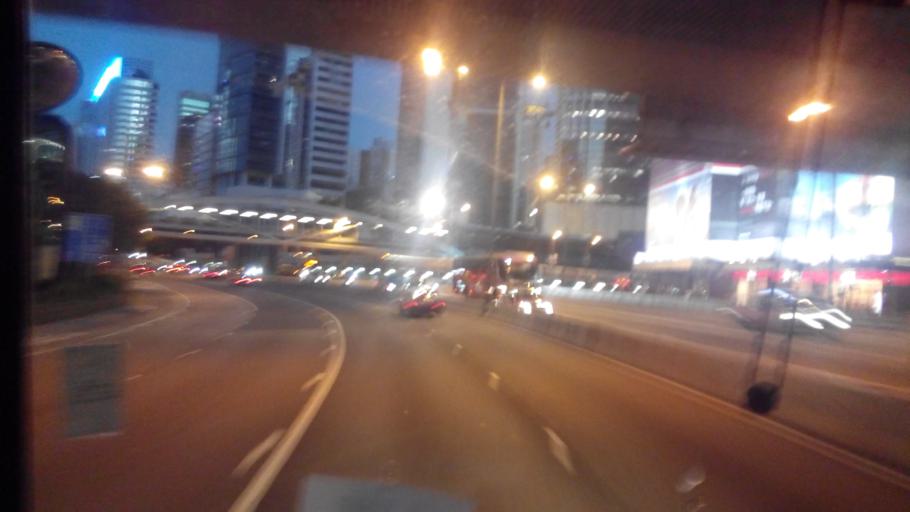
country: HK
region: Central and Western
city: Central
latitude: 22.2797
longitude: 114.1651
